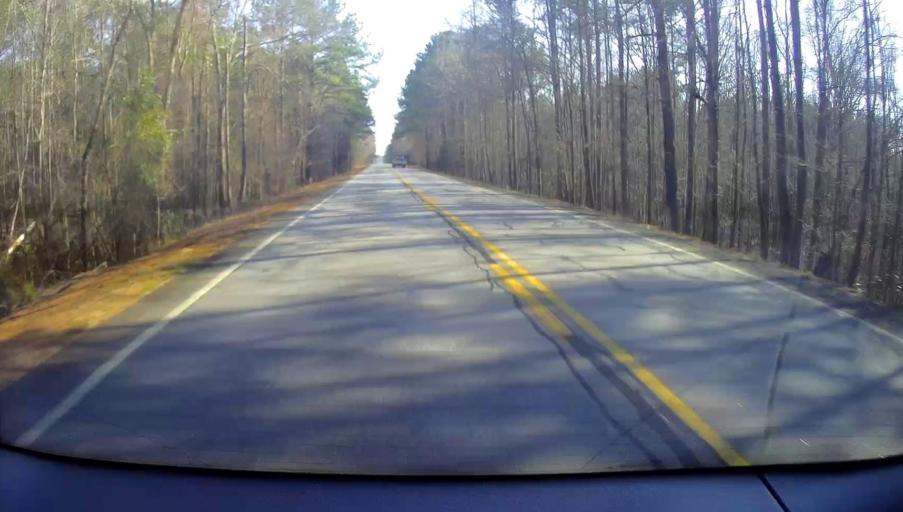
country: US
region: Georgia
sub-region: Butts County
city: Indian Springs
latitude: 33.2079
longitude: -83.8589
